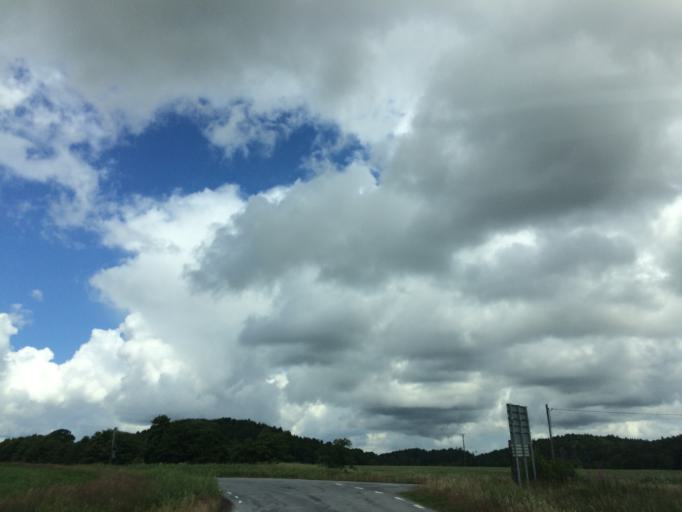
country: SE
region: Vaestra Goetaland
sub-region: Munkedals Kommun
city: Munkedal
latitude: 58.4409
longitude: 11.6494
